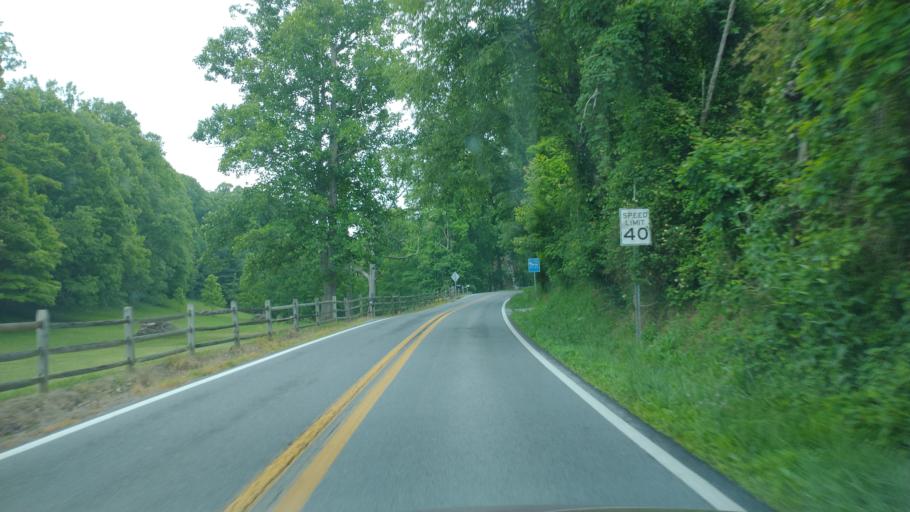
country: US
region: West Virginia
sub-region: Mercer County
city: Athens
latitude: 37.4066
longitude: -81.0333
